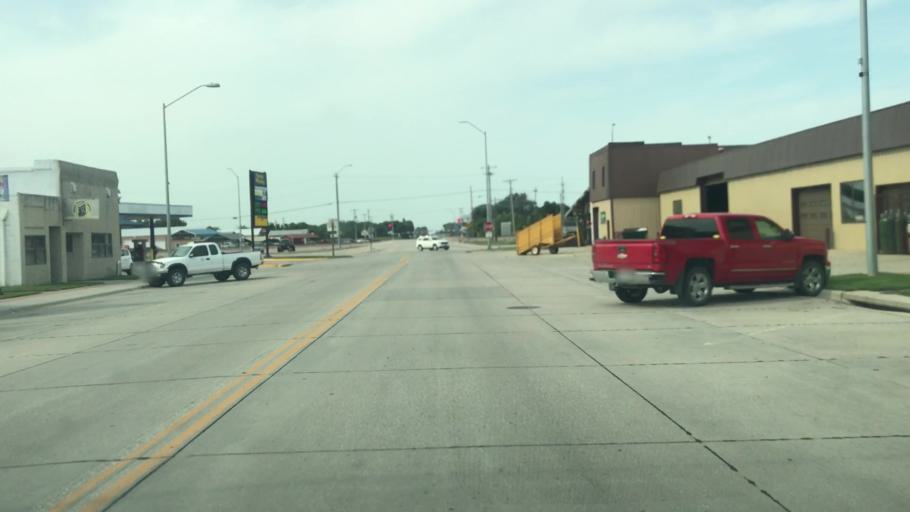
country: US
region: Nebraska
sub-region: Hall County
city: Wood River
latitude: 41.0010
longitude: -98.6074
